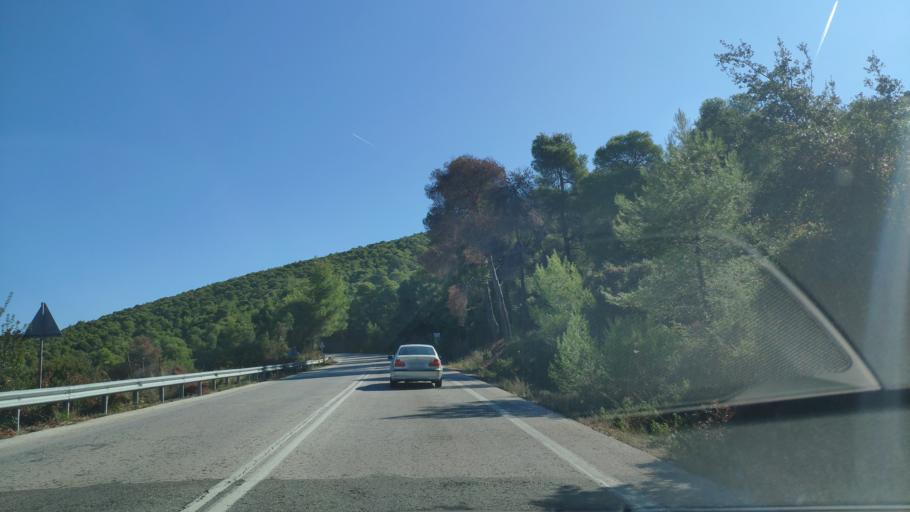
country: GR
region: Peloponnese
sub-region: Nomos Korinthias
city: Sofikon
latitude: 37.8275
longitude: 23.0903
